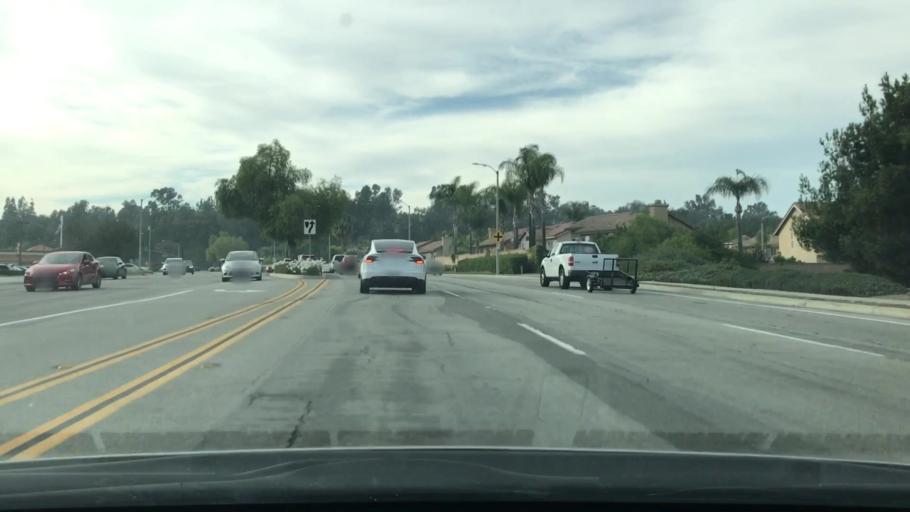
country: US
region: California
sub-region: San Bernardino County
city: Chino Hills
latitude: 34.0109
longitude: -117.7399
